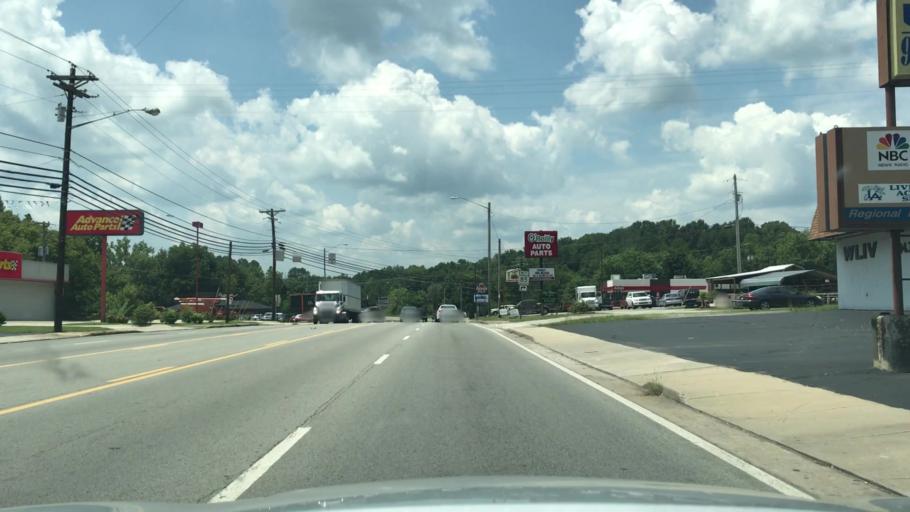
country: US
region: Tennessee
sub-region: Overton County
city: Livingston
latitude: 36.3772
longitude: -85.3367
